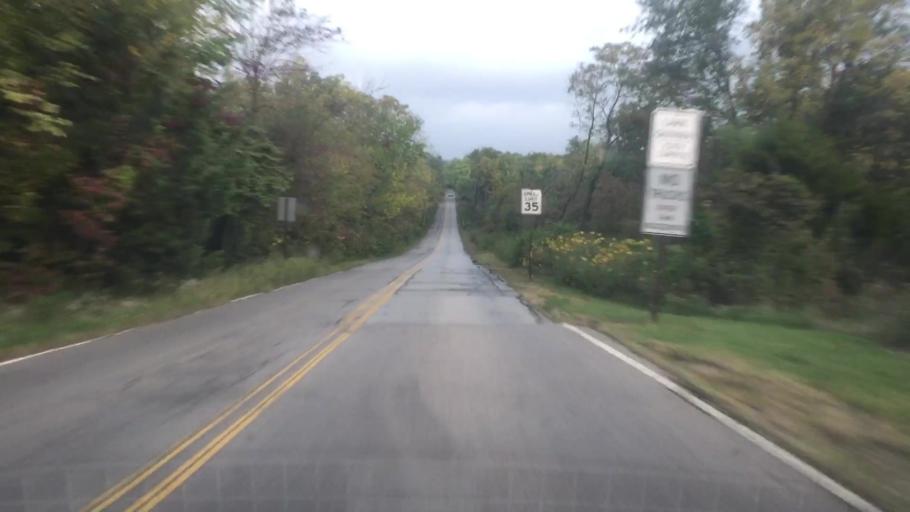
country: US
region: Kansas
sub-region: Johnson County
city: Shawnee
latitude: 39.0473
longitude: -94.7614
